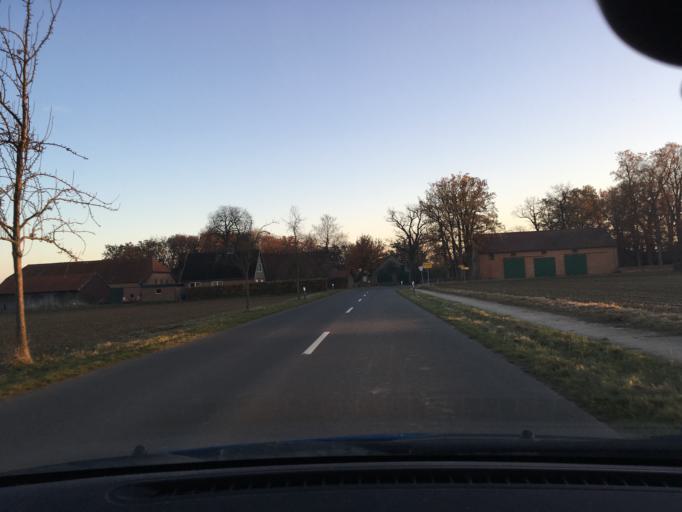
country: DE
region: Lower Saxony
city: Natendorf
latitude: 53.0594
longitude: 10.4541
